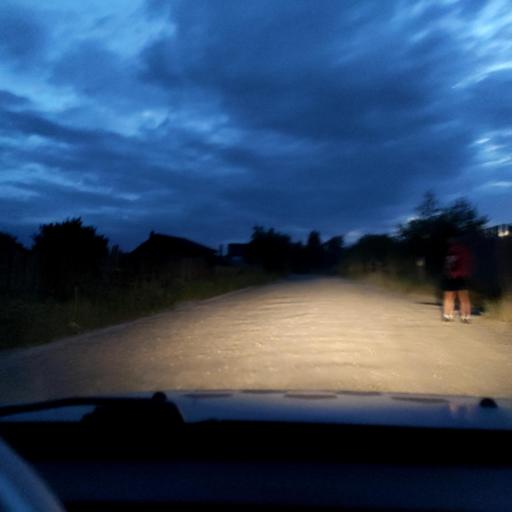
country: RU
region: Perm
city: Kondratovo
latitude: 58.0291
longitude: 56.0669
